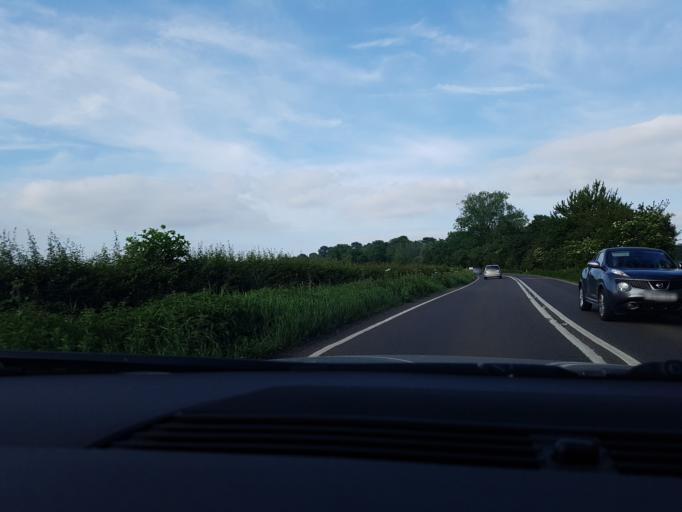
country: GB
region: England
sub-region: Northamptonshire
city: Deanshanger
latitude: 52.0216
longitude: -0.9181
